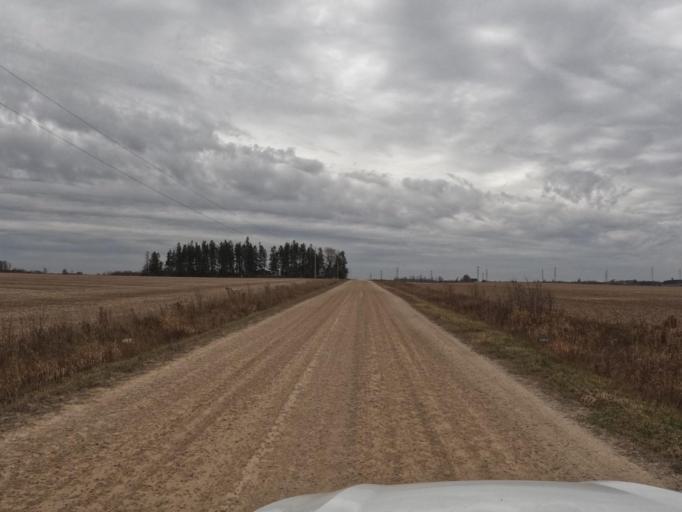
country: CA
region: Ontario
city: Shelburne
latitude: 44.0042
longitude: -80.3879
